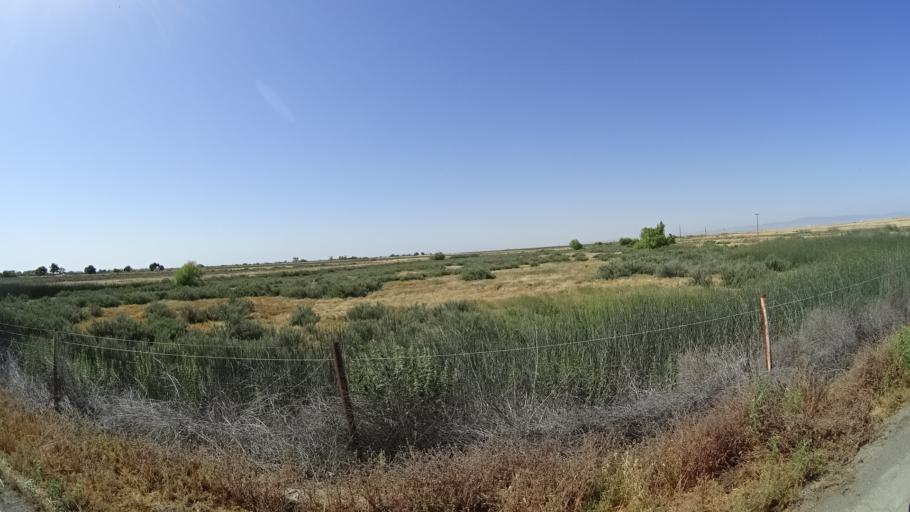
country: US
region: California
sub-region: Kings County
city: Lemoore Station
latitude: 36.2505
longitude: -119.8607
